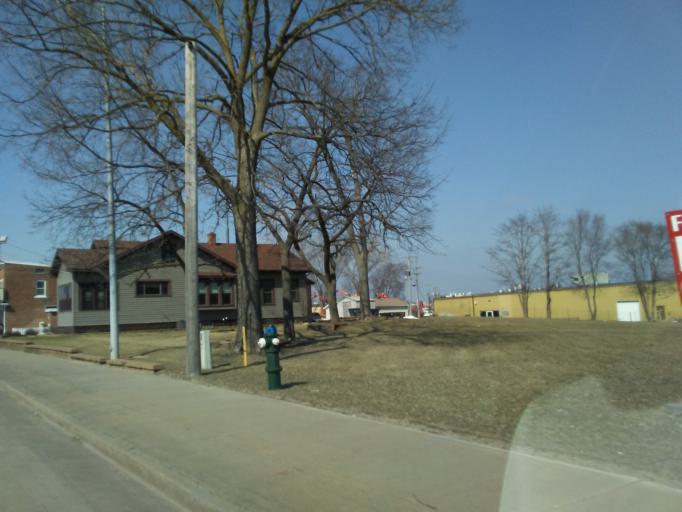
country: US
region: Wisconsin
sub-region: La Crosse County
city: La Crosse
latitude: 43.7804
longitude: -91.2255
